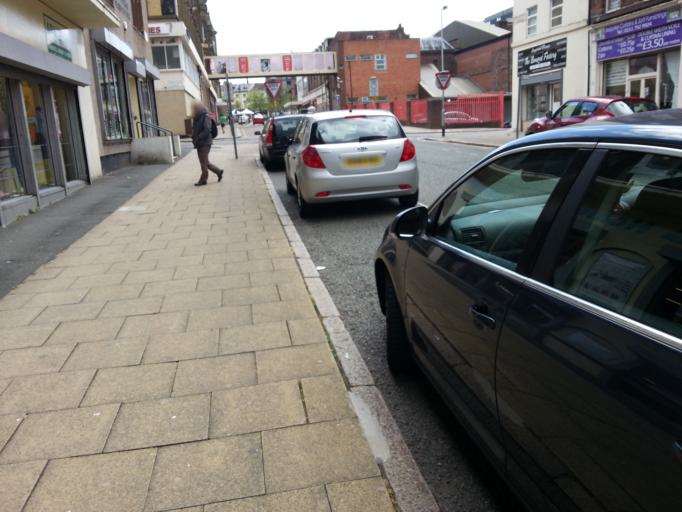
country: GB
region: England
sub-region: Liverpool
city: Liverpool
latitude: 53.4107
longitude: -2.9730
